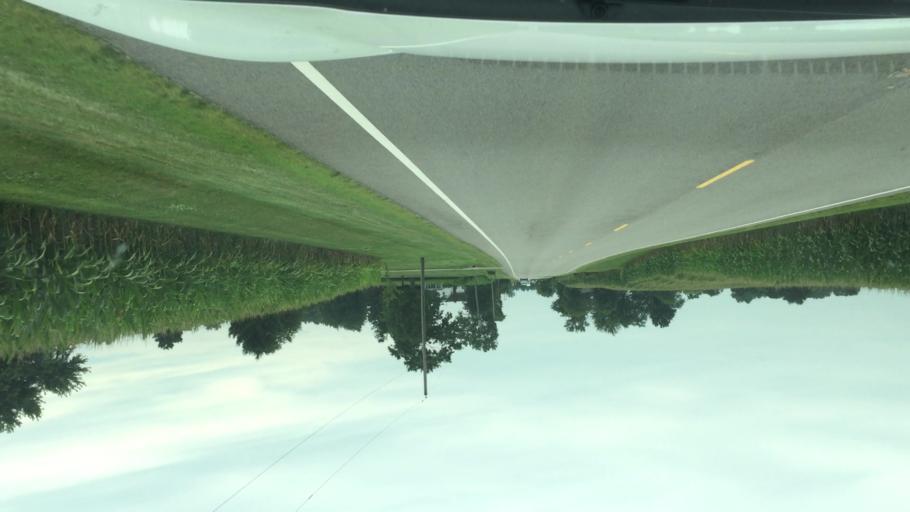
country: US
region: Ohio
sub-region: Champaign County
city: Mechanicsburg
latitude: 40.1295
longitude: -83.4870
